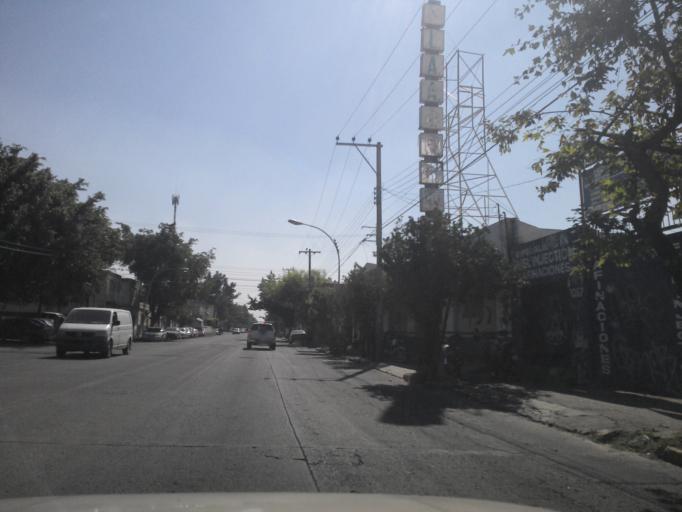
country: MX
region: Jalisco
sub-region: Zapopan
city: Zapopan
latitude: 20.6949
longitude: -103.3584
